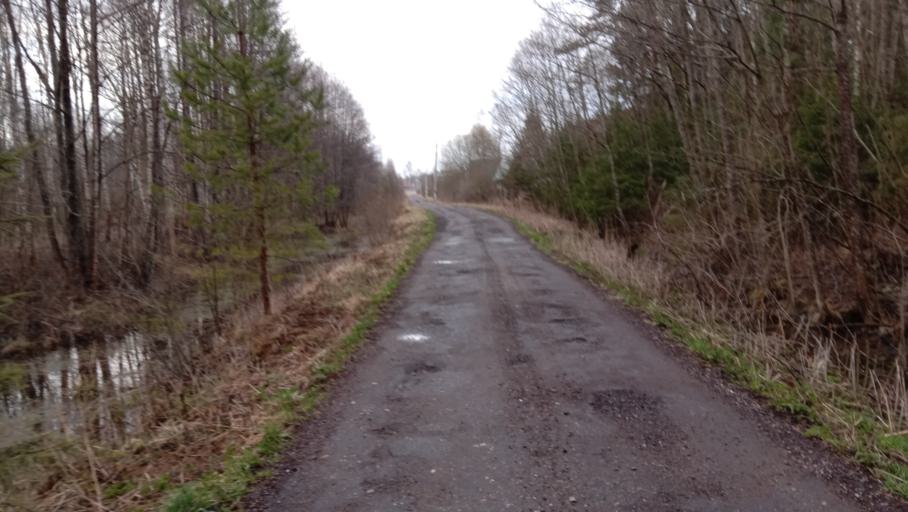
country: RU
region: Moskovskaya
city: Uvarovka
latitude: 55.7645
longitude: 35.7922
